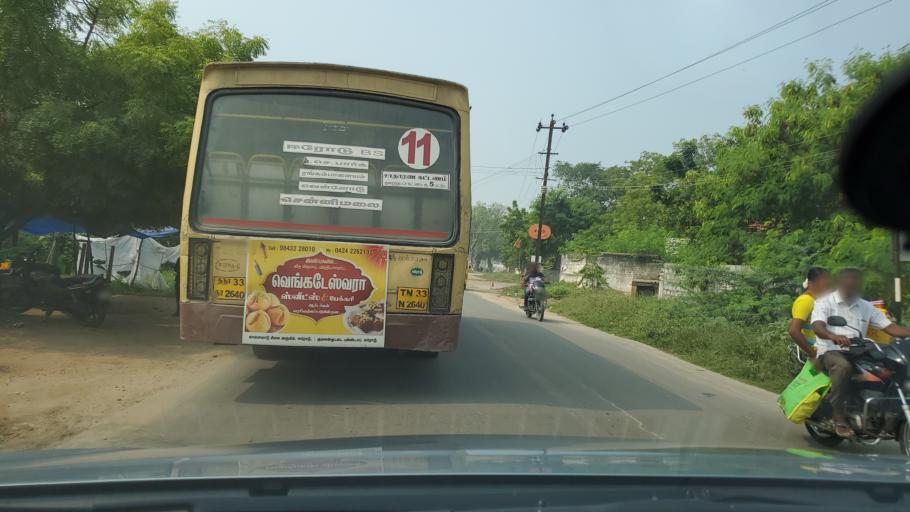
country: IN
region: Tamil Nadu
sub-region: Erode
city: Erode
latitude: 11.3139
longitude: 77.7102
